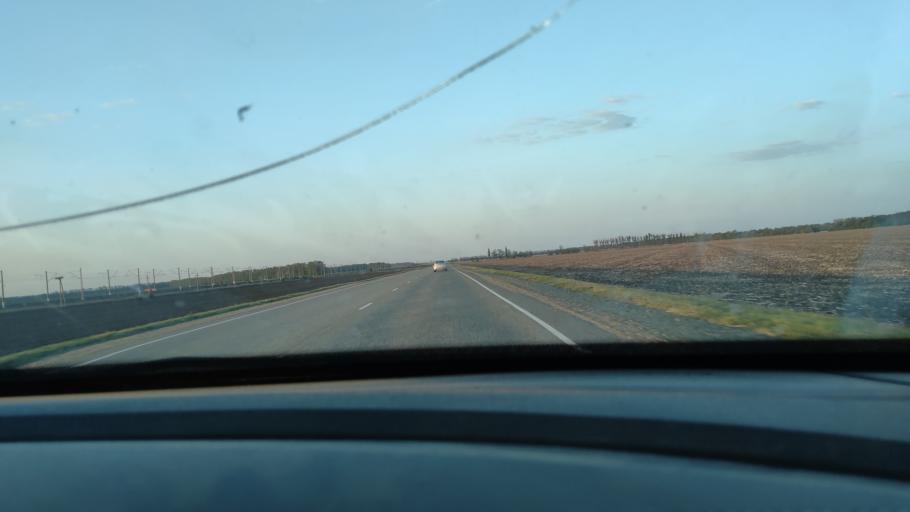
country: RU
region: Krasnodarskiy
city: Novominskaya
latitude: 46.3513
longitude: 38.9614
